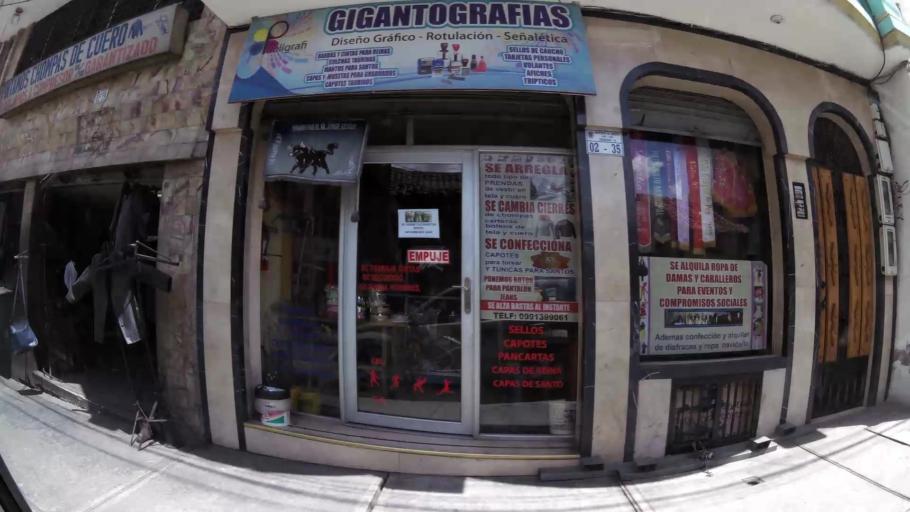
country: EC
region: Tungurahua
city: Ambato
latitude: -1.2451
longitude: -78.6263
